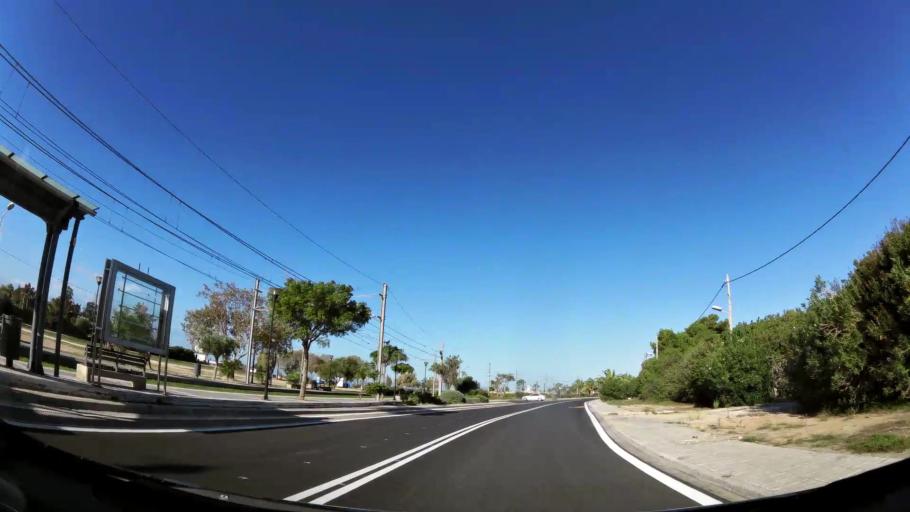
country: GR
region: Attica
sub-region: Nomarchia Athinas
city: Elliniko
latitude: 37.8678
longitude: 23.7387
